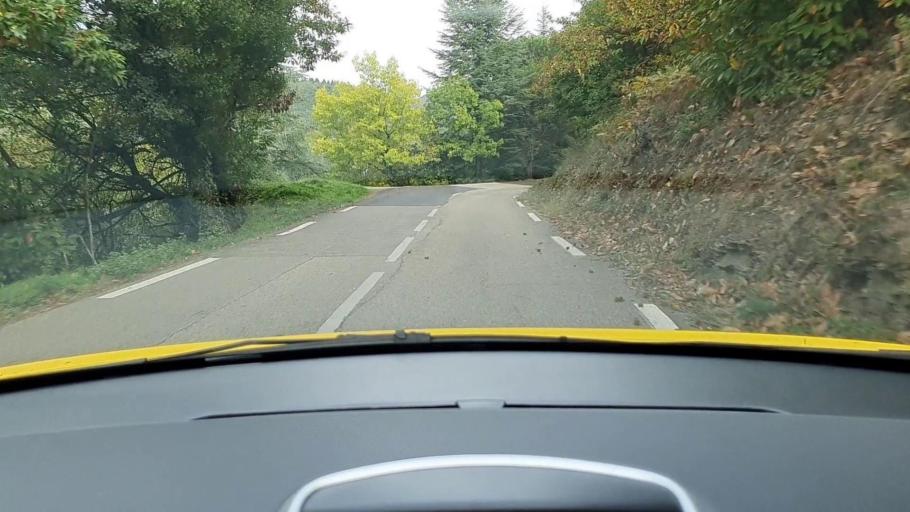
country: FR
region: Languedoc-Roussillon
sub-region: Departement du Gard
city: Le Vigan
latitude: 44.0001
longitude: 3.5893
